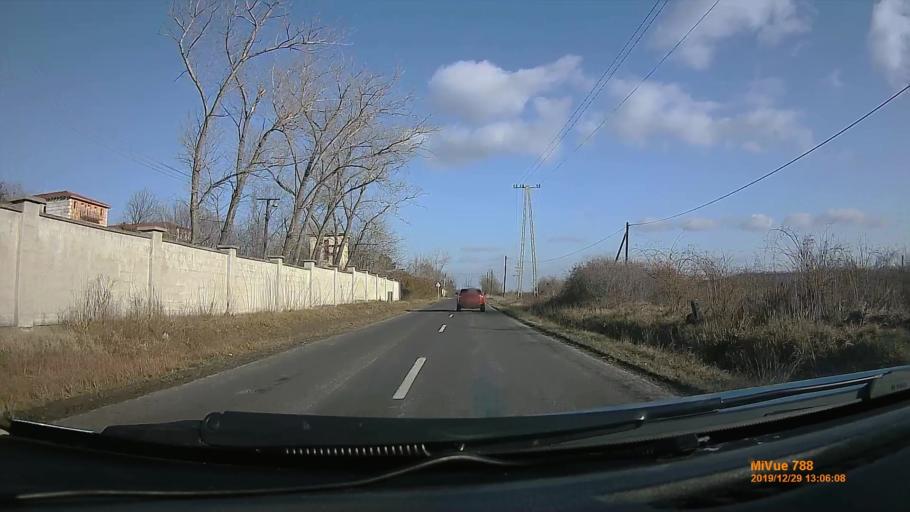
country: HU
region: Heves
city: Abasar
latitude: 47.8069
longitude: 20.0237
